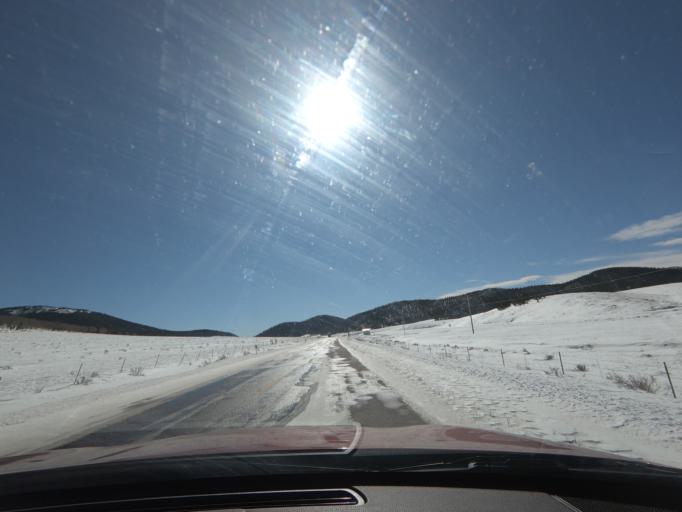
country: US
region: Colorado
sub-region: Teller County
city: Cripple Creek
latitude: 38.7707
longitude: -105.1196
